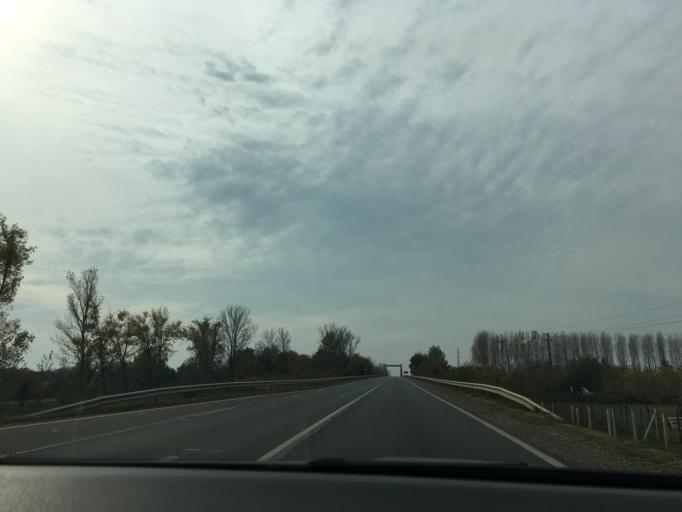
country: HU
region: Hajdu-Bihar
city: Hajduszoboszlo
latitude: 47.4216
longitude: 21.3523
